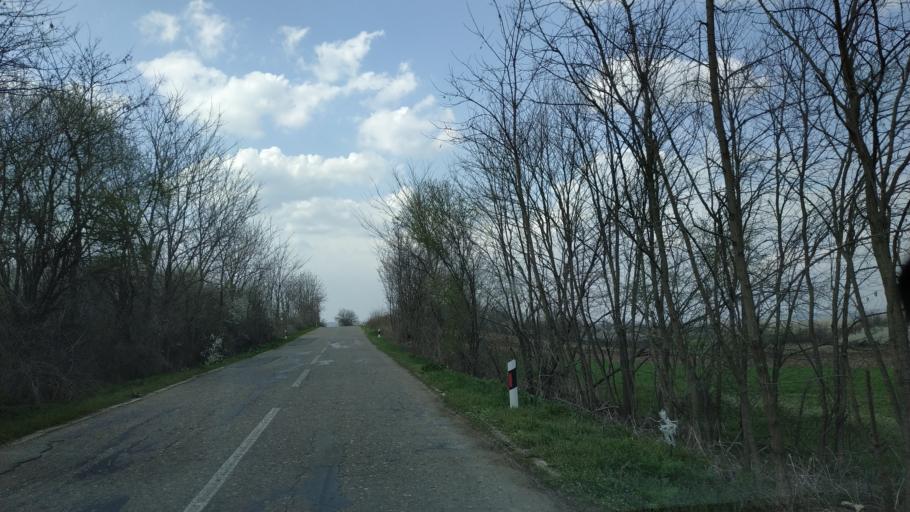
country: RS
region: Central Serbia
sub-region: Nisavski Okrug
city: Aleksinac
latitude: 43.5621
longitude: 21.6009
